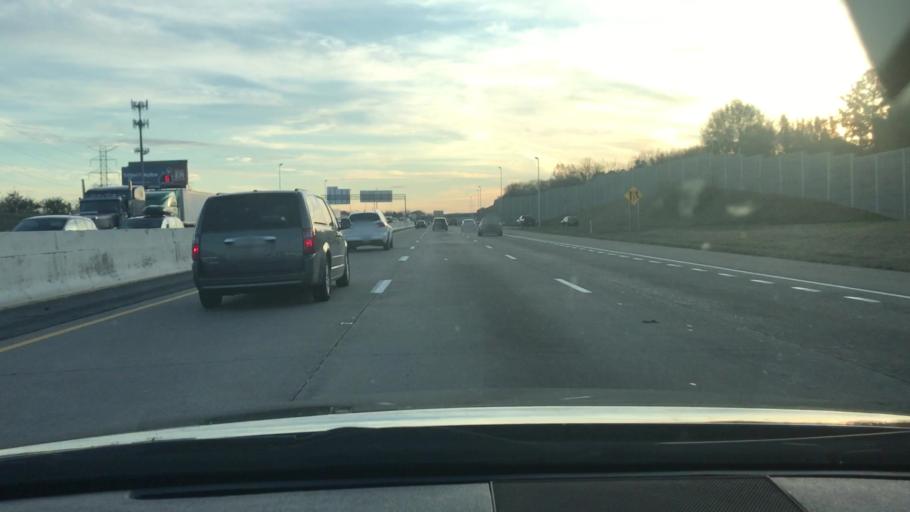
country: US
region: Tennessee
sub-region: Davidson County
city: Goodlettsville
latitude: 36.3024
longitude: -86.7097
